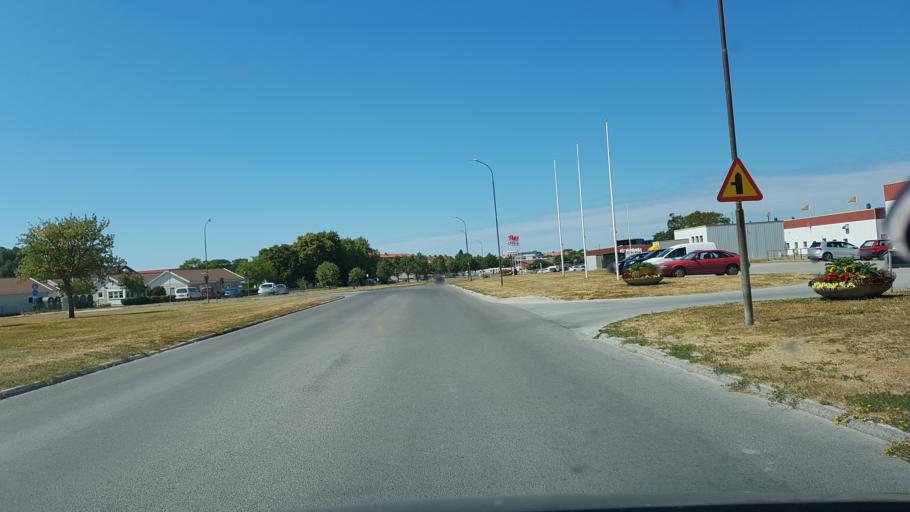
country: SE
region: Gotland
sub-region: Gotland
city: Visby
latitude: 57.6415
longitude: 18.3211
